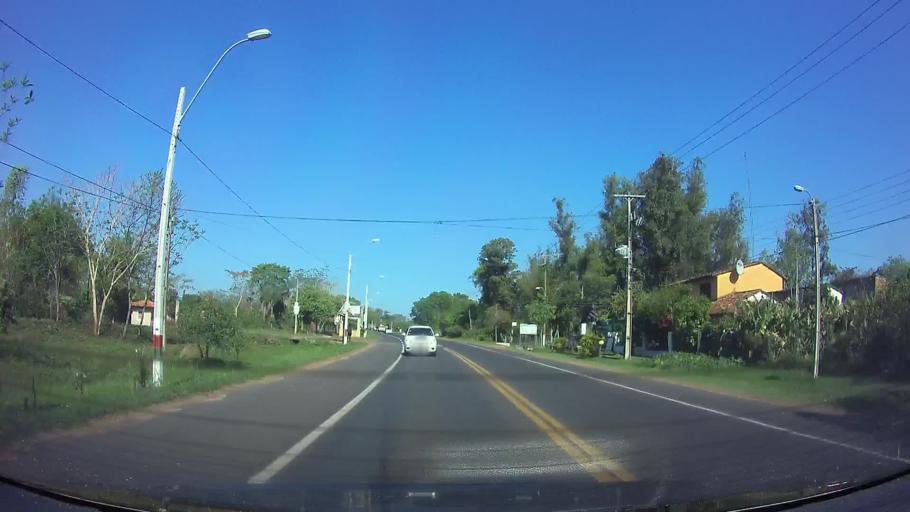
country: PY
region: Central
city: Aregua
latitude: -25.3243
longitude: -57.3659
